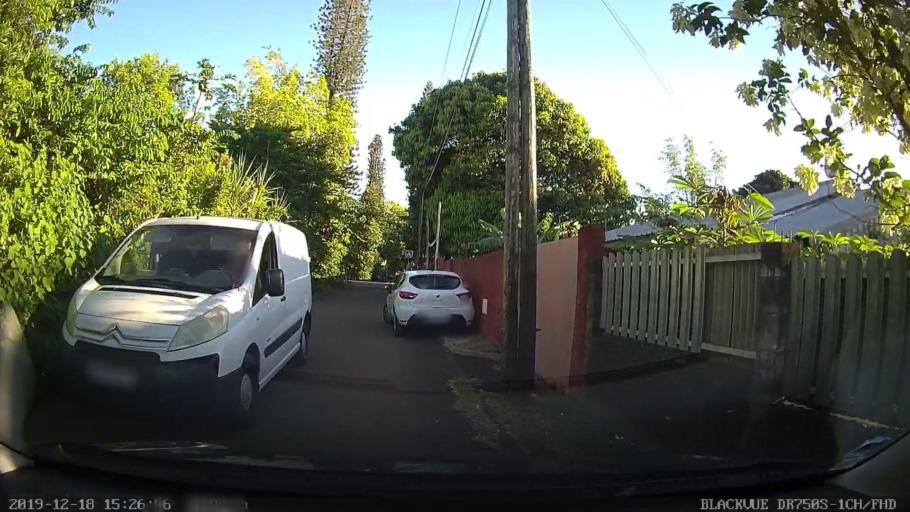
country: RE
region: Reunion
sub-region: Reunion
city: Bras-Panon
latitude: -21.0008
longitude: 55.6535
